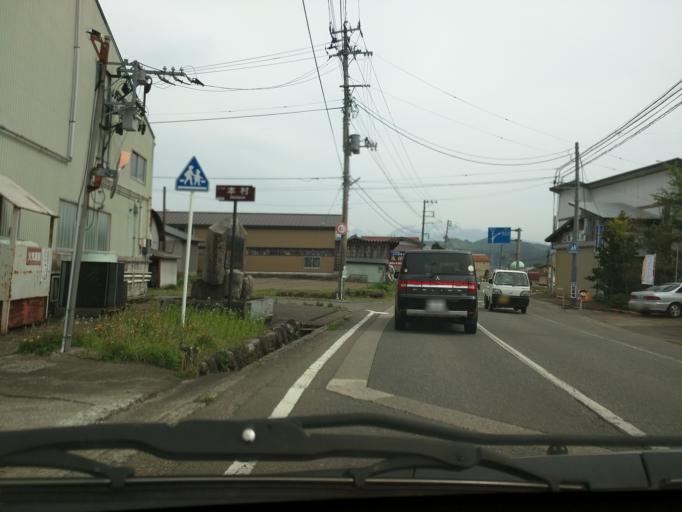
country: JP
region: Niigata
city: Ojiya
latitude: 37.2501
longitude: 138.9299
